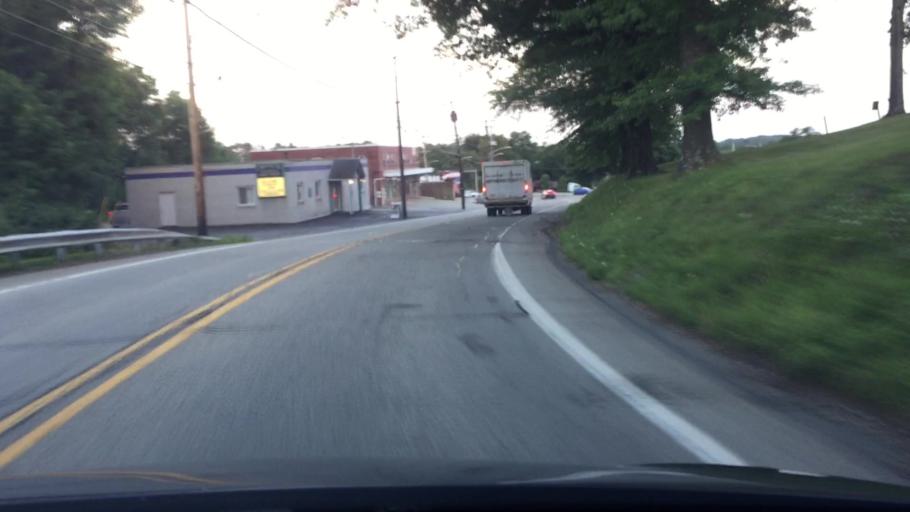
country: US
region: Pennsylvania
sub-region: Allegheny County
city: Churchill
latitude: 40.4612
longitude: -79.8452
